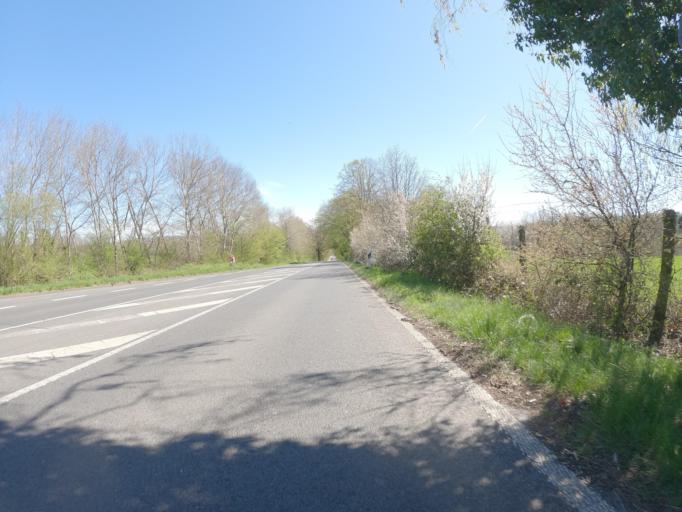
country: DE
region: North Rhine-Westphalia
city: Stolberg
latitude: 50.7742
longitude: 6.1917
